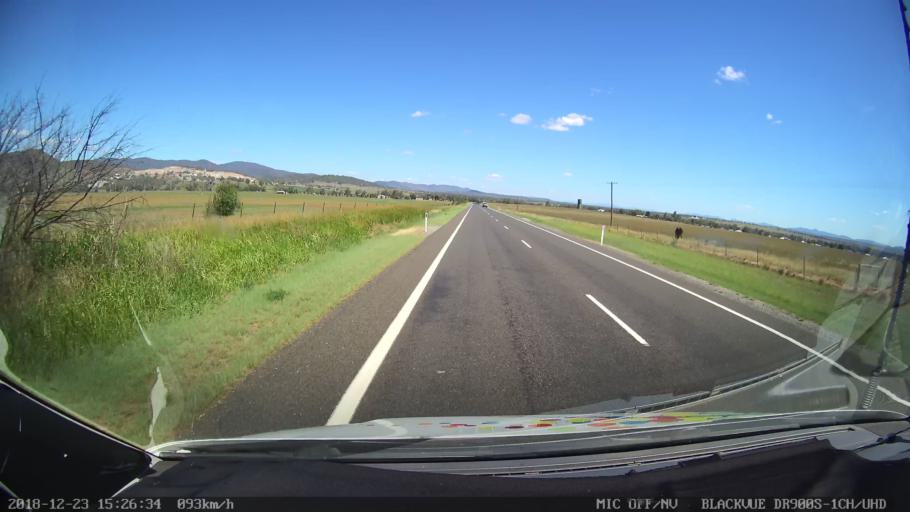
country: AU
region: New South Wales
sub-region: Tamworth Municipality
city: East Tamworth
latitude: -30.9184
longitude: 150.8393
